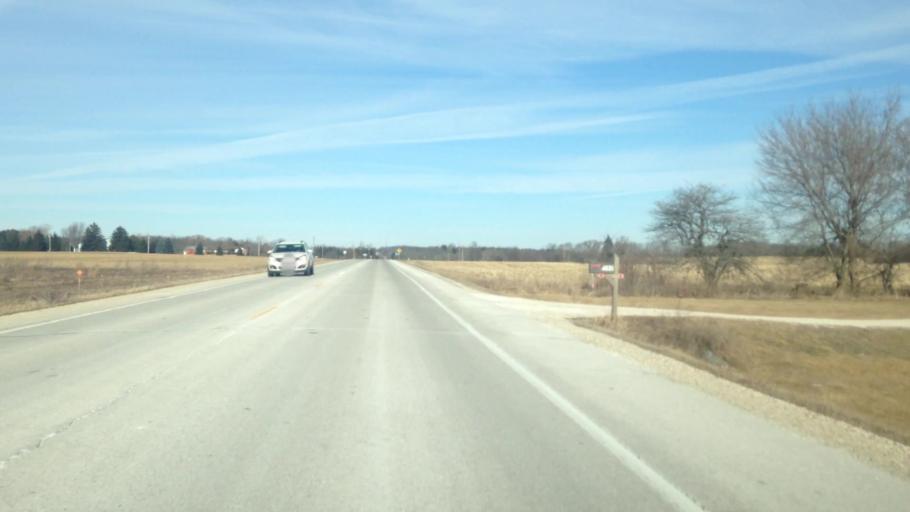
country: US
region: Wisconsin
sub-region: Washington County
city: Slinger
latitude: 43.2762
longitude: -88.2613
